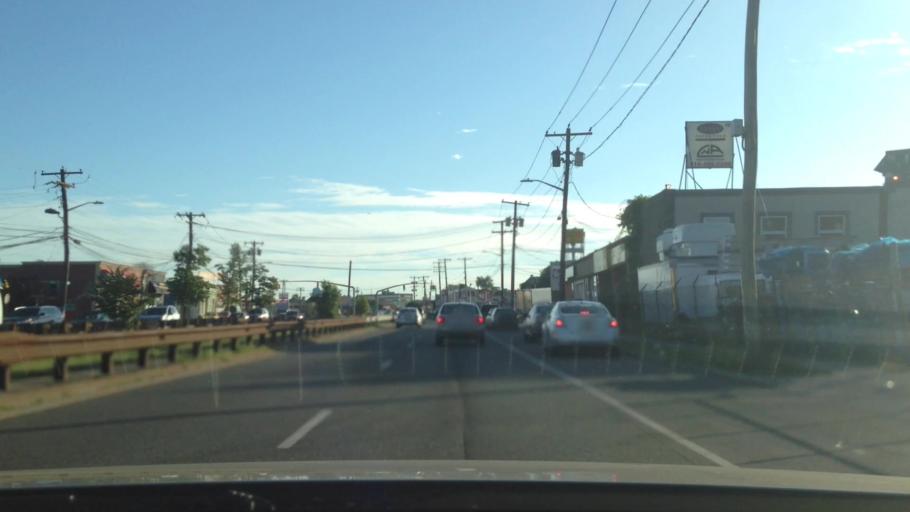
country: US
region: New York
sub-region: Nassau County
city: Hempstead
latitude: 40.7007
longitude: -73.6275
